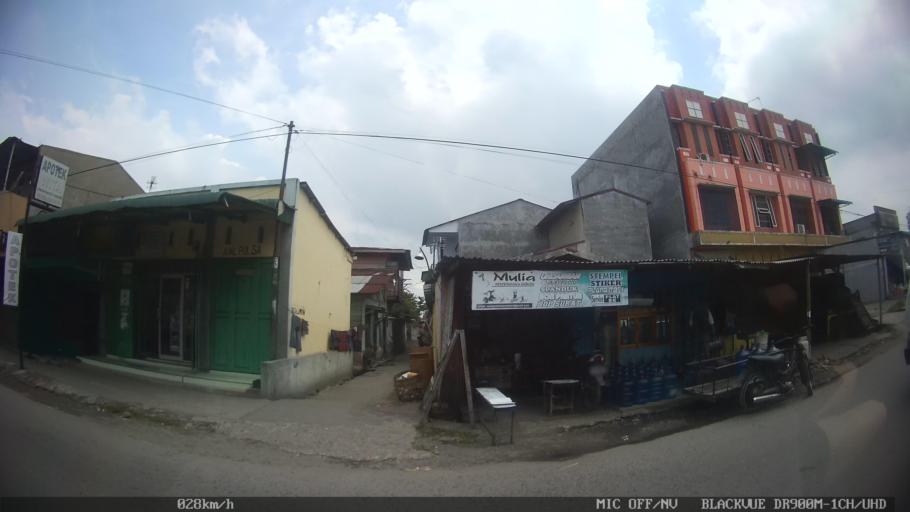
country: ID
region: North Sumatra
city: Medan
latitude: 3.6428
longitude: 98.6739
